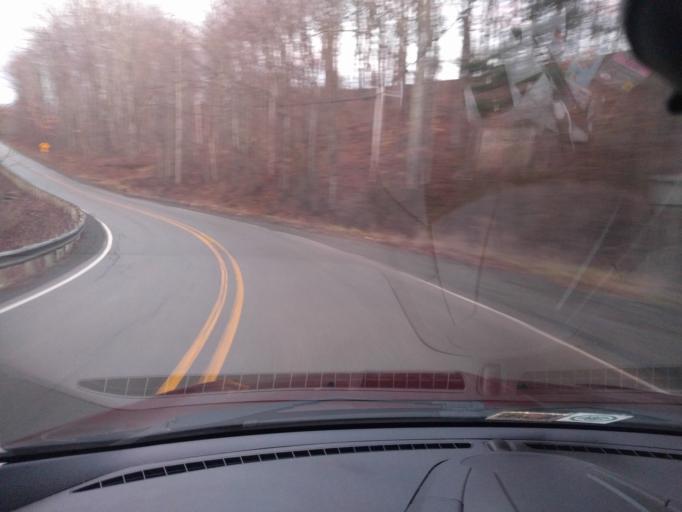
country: US
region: West Virginia
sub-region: Greenbrier County
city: Rainelle
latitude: 37.9980
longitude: -80.8733
